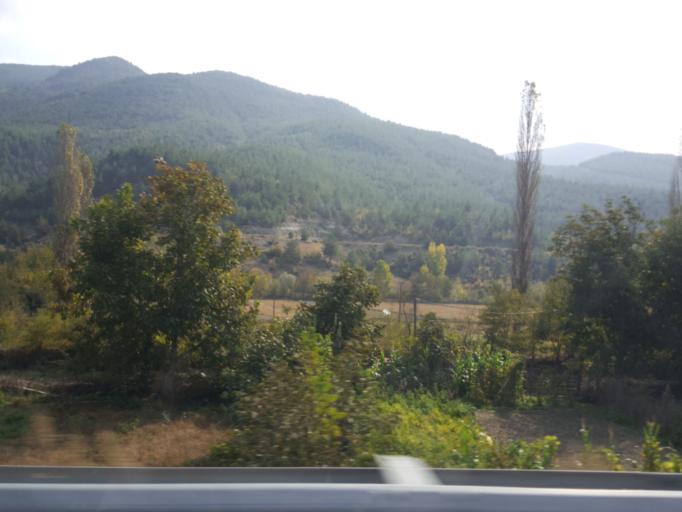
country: TR
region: Sinop
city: Sarayduzu
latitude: 41.3877
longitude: 34.9381
